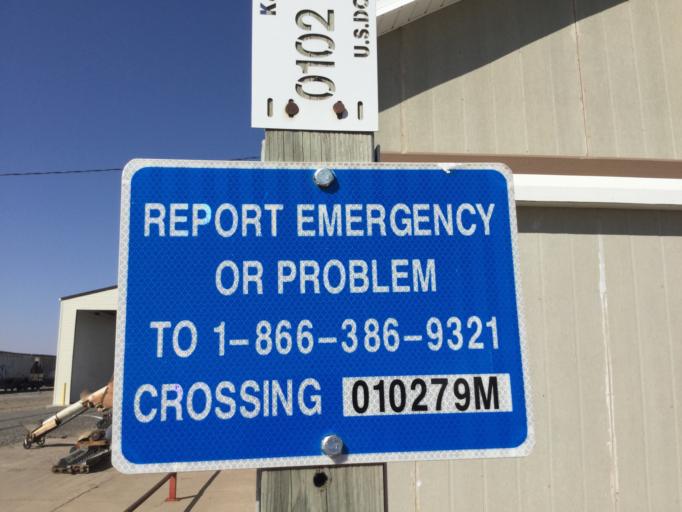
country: US
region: Kansas
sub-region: Rush County
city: La Crosse
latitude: 38.4672
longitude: -99.3188
